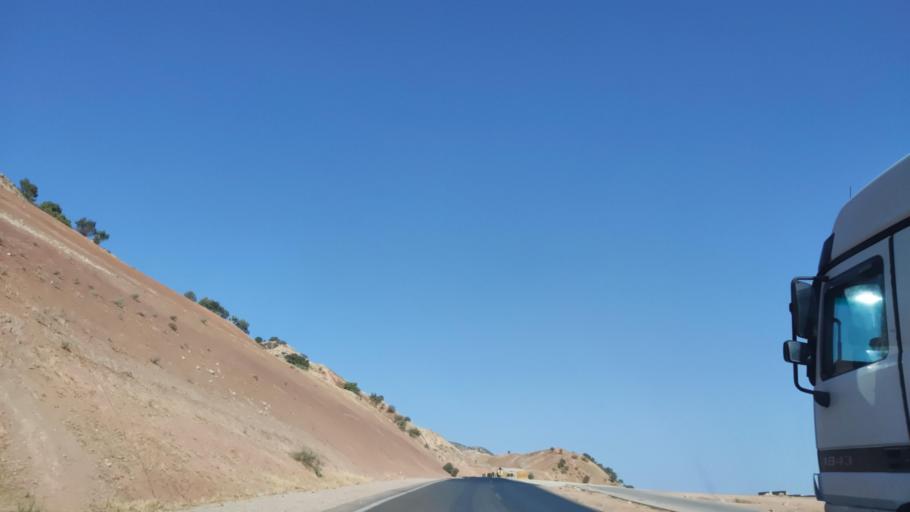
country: IQ
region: Arbil
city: Shaqlawah
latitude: 36.4333
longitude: 44.3035
